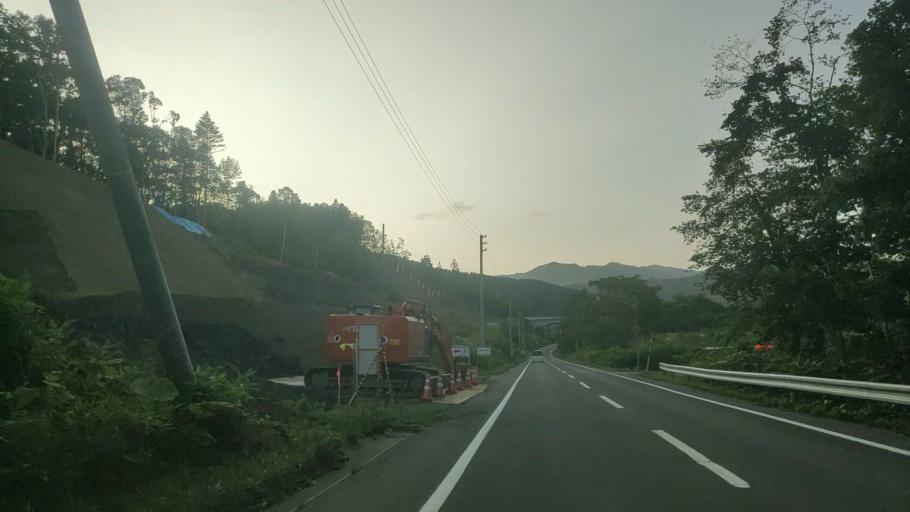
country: JP
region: Hokkaido
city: Bibai
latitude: 43.2240
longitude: 142.0477
